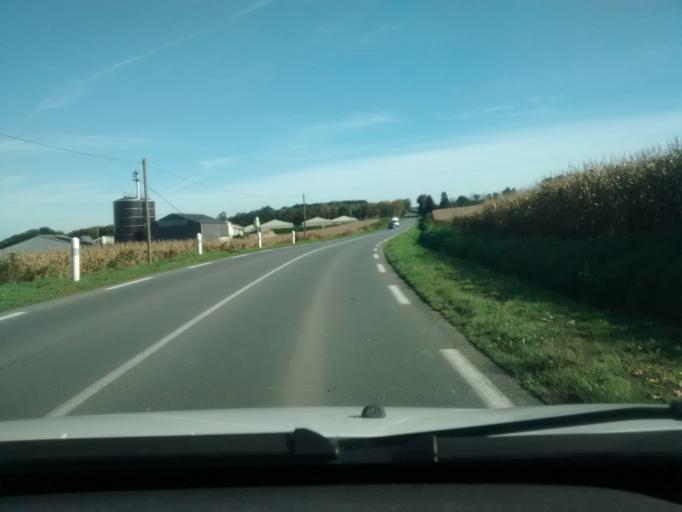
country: FR
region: Brittany
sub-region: Departement des Cotes-d'Armor
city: Langoat
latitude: 48.7627
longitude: -3.2891
